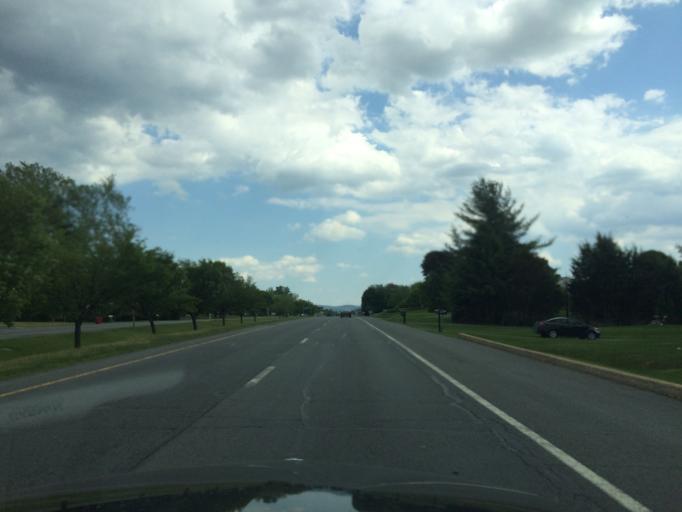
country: US
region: Maryland
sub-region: Washington County
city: Hagerstown
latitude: 39.6224
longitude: -77.6963
